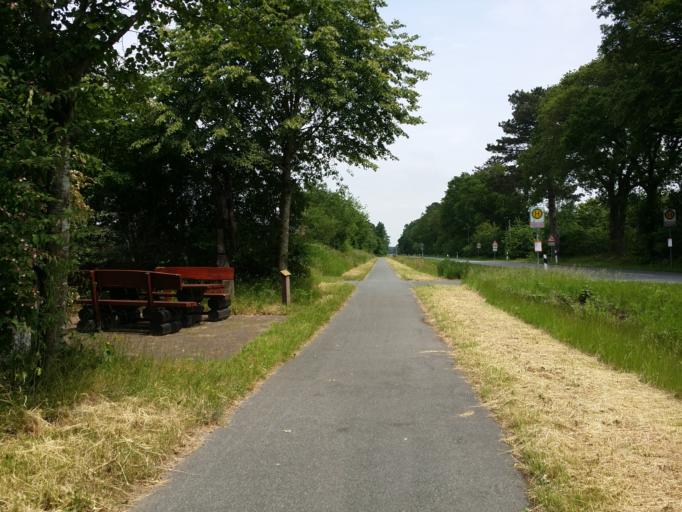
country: DE
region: Lower Saxony
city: Friedeburg
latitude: 53.4132
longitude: 7.8914
